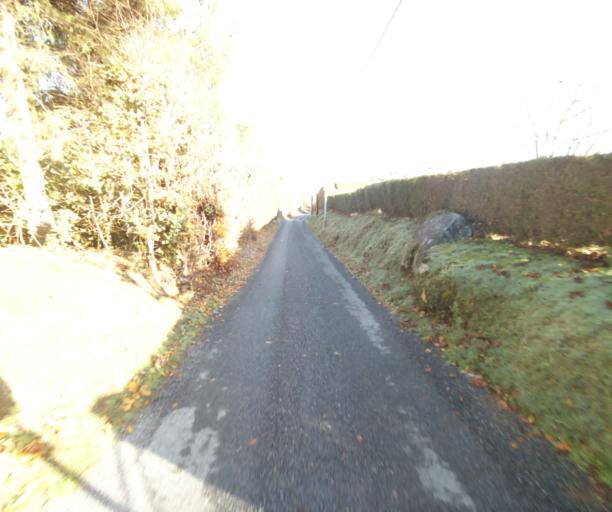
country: FR
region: Limousin
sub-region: Departement de la Correze
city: Laguenne
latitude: 45.2438
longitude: 1.7579
